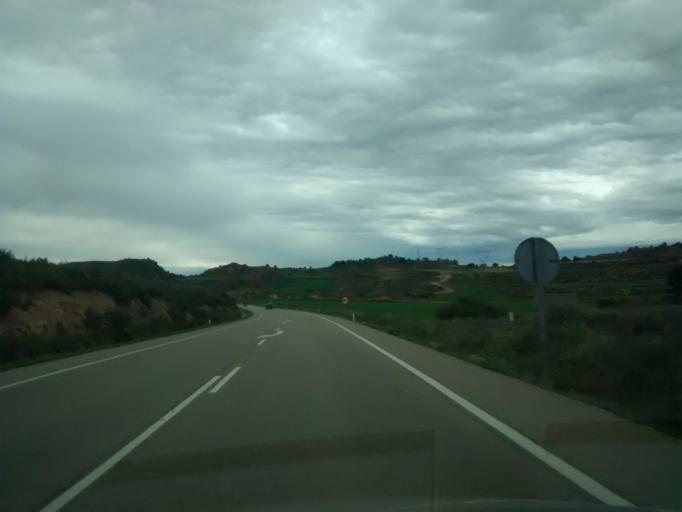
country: ES
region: Aragon
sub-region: Provincia de Zaragoza
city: Caspe
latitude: 41.2065
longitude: 0.0368
